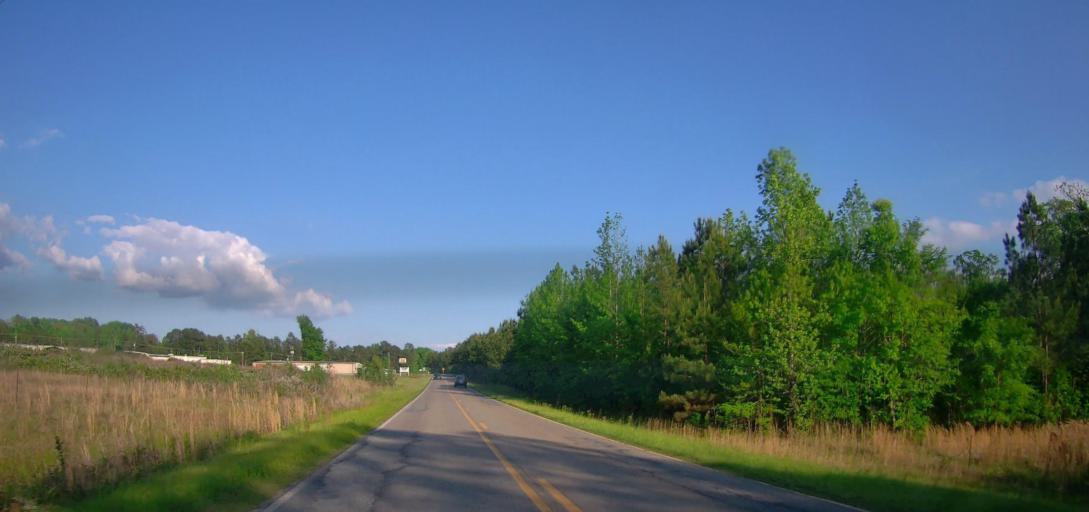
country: US
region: Georgia
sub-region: Putnam County
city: Eatonton
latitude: 33.2731
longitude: -83.3056
